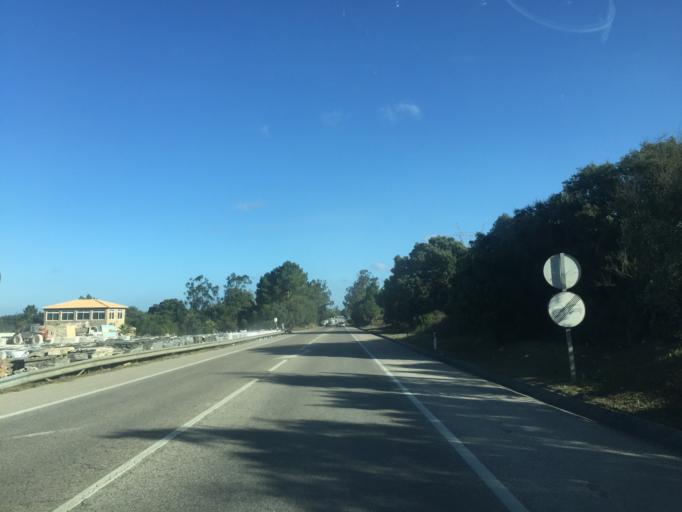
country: PT
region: Leiria
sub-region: Alcobaca
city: Turquel
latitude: 39.4563
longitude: -8.9472
